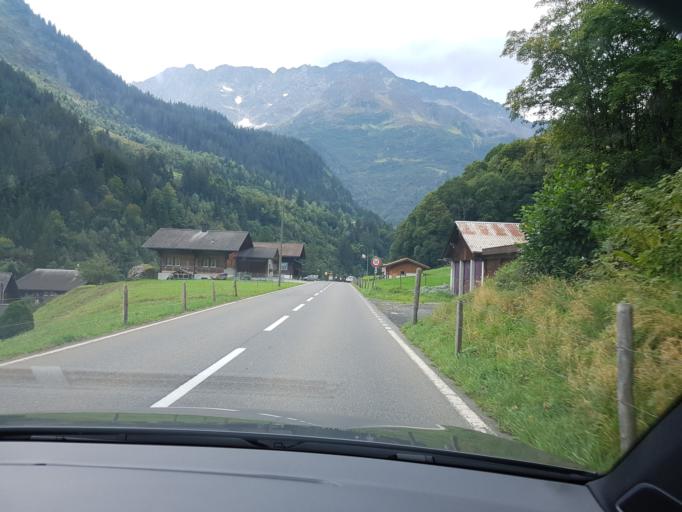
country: CH
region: Obwalden
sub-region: Obwalden
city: Engelberg
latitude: 46.7291
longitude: 8.3320
